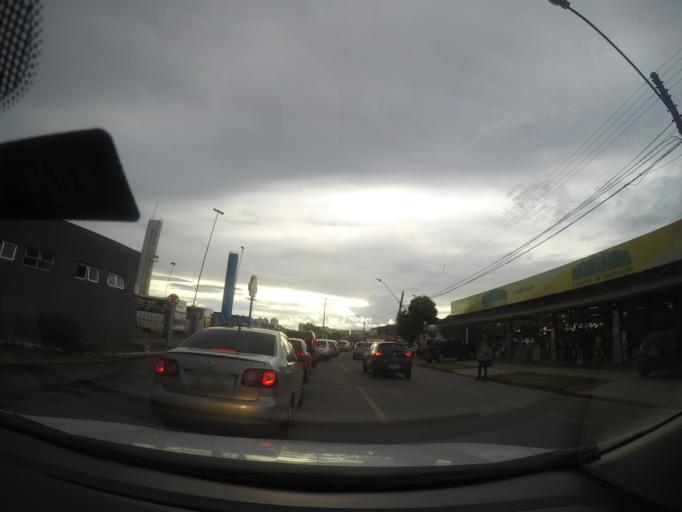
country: BR
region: Goias
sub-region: Goiania
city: Goiania
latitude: -16.7092
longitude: -49.3103
